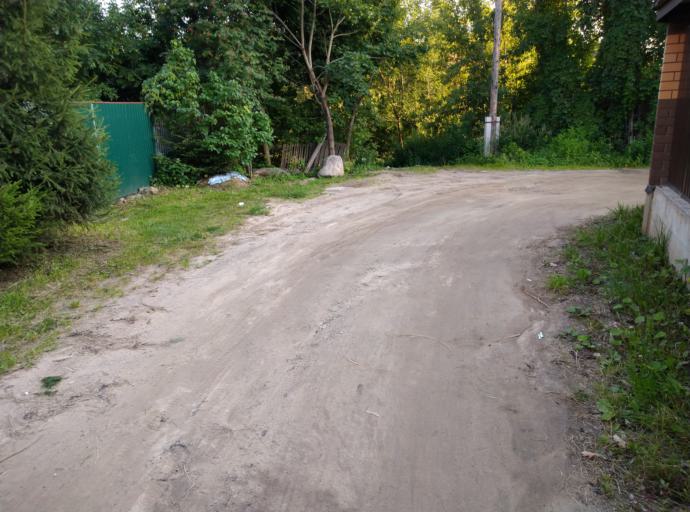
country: RU
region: Kostroma
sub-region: Kostromskoy Rayon
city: Kostroma
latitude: 57.7513
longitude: 40.9576
